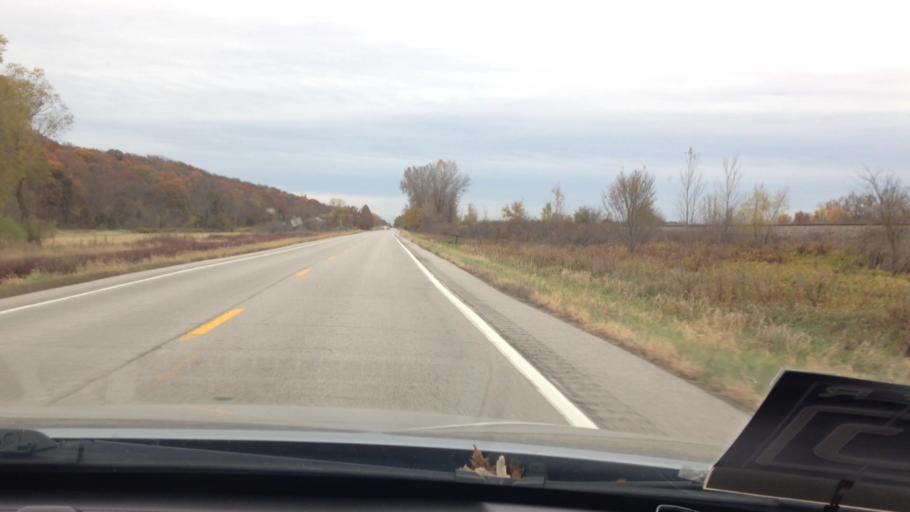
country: US
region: Kansas
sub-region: Leavenworth County
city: Leavenworth
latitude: 39.3414
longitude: -94.8624
